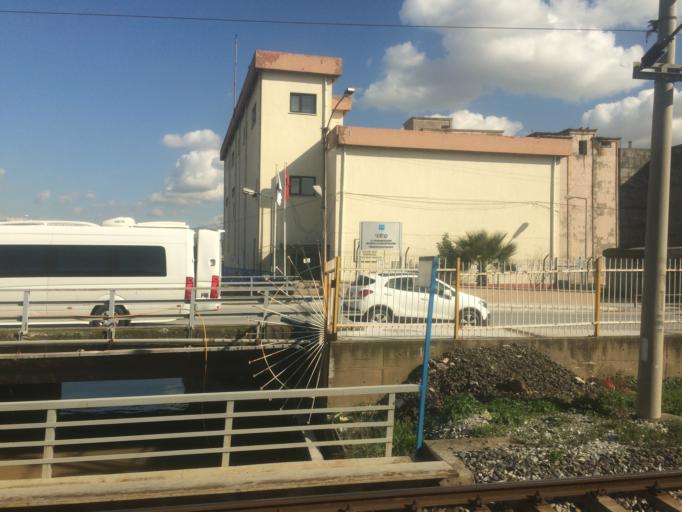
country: TR
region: Izmir
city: Izmir
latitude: 38.4602
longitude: 27.1669
